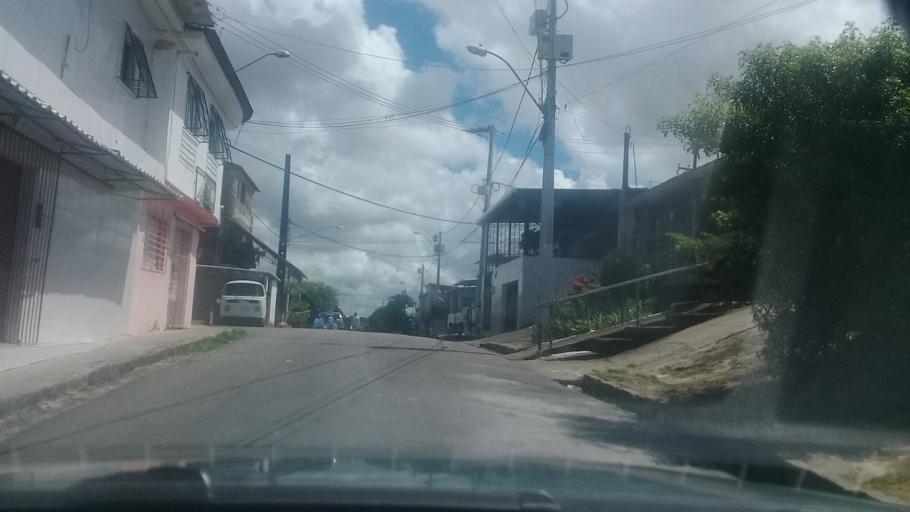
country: BR
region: Pernambuco
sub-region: Jaboatao Dos Guararapes
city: Jaboatao dos Guararapes
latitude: -8.1232
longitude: -34.9468
